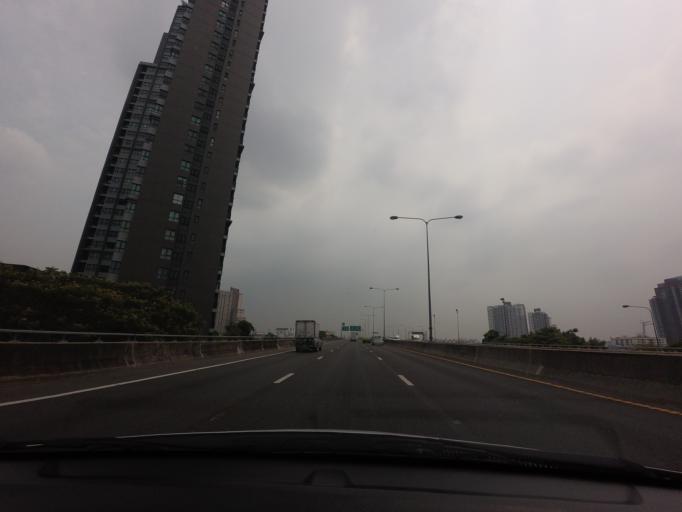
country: TH
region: Bangkok
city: Phra Khanong
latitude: 13.7136
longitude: 100.5998
